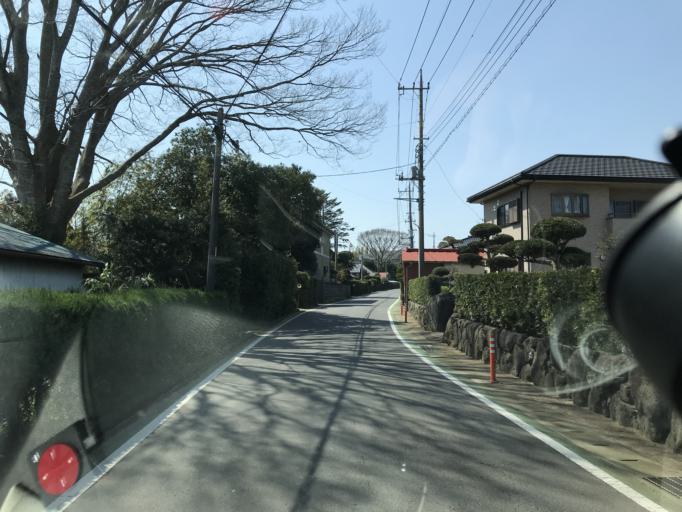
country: JP
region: Chiba
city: Asahi
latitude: 35.7903
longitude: 140.6845
